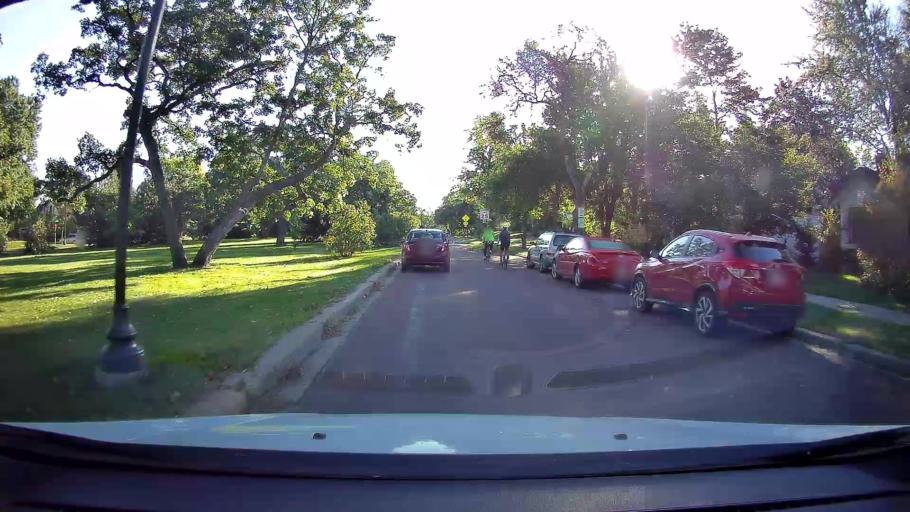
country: US
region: Minnesota
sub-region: Hennepin County
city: Richfield
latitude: 44.9161
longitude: -93.2317
